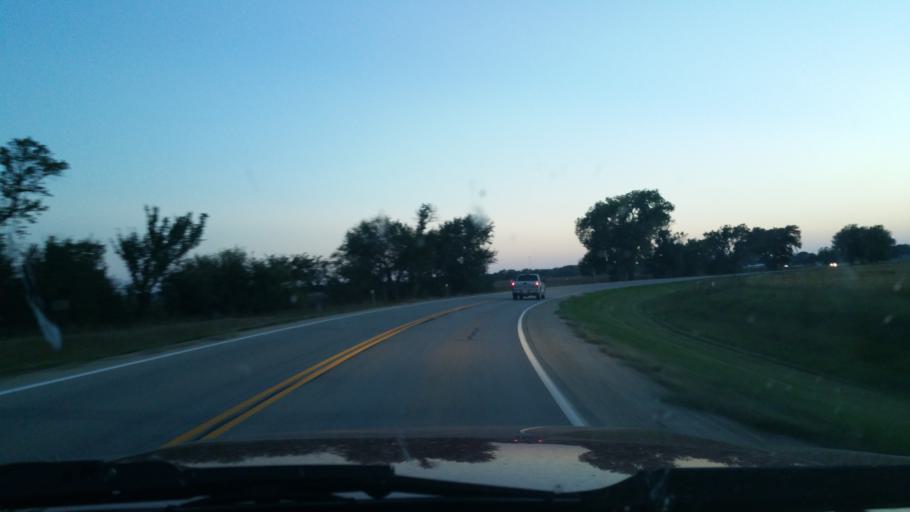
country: US
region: Kansas
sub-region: Riley County
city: Manhattan
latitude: 39.2353
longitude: -96.5714
